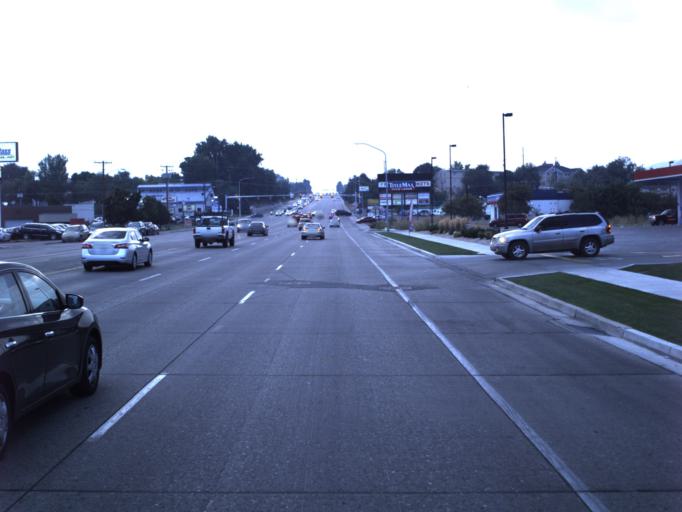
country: US
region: Utah
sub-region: Utah County
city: Provo
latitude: 40.2545
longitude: -111.6704
